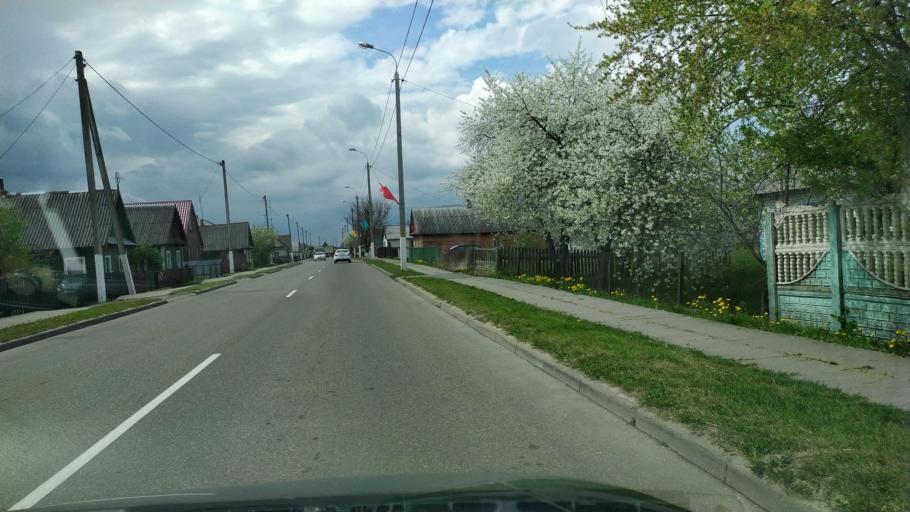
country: BY
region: Brest
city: Pruzhany
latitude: 52.5557
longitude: 24.4424
